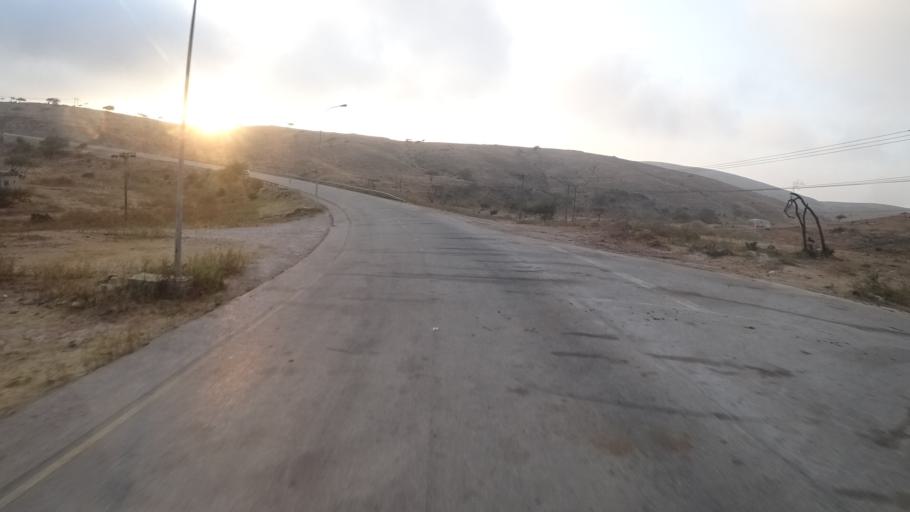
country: OM
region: Zufar
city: Salalah
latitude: 17.1400
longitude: 53.9692
